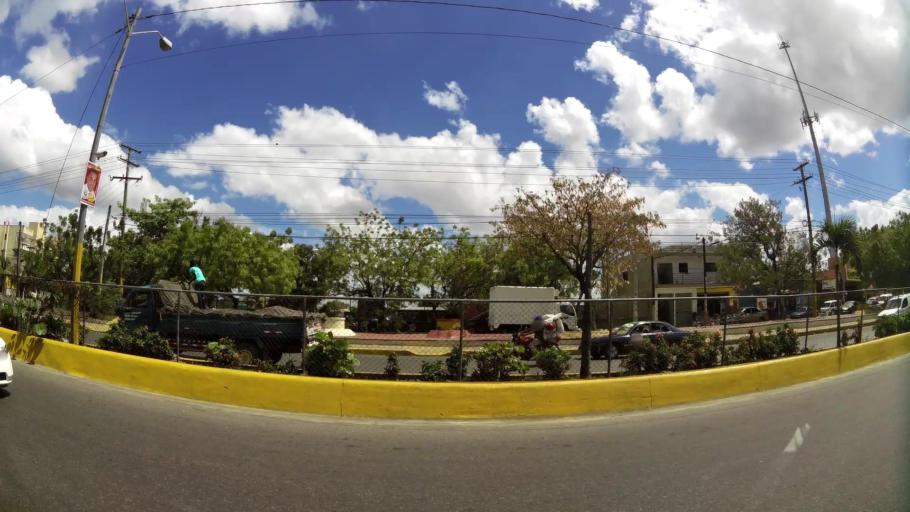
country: DO
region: Nacional
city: Ensanche Luperon
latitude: 18.5194
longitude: -69.9149
